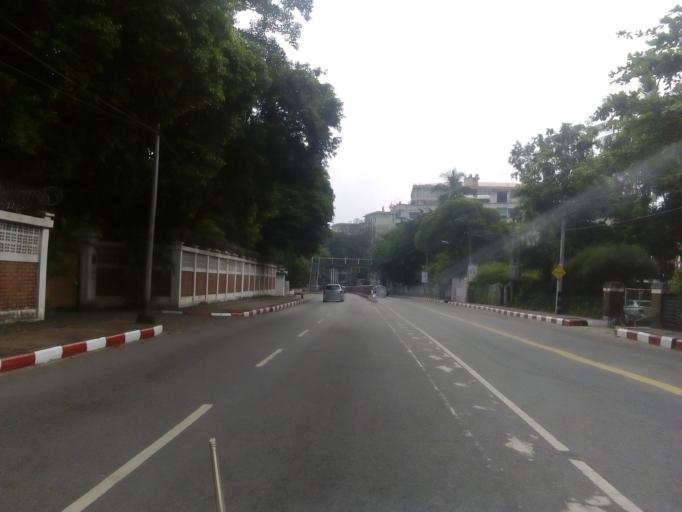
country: MM
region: Yangon
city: Yangon
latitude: 16.7855
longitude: 96.1567
